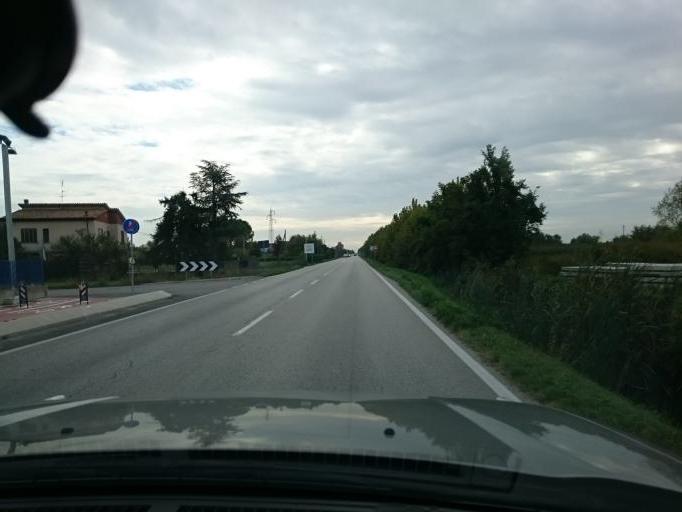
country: IT
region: Veneto
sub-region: Provincia di Padova
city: Legnaro
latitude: 45.3389
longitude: 11.9737
